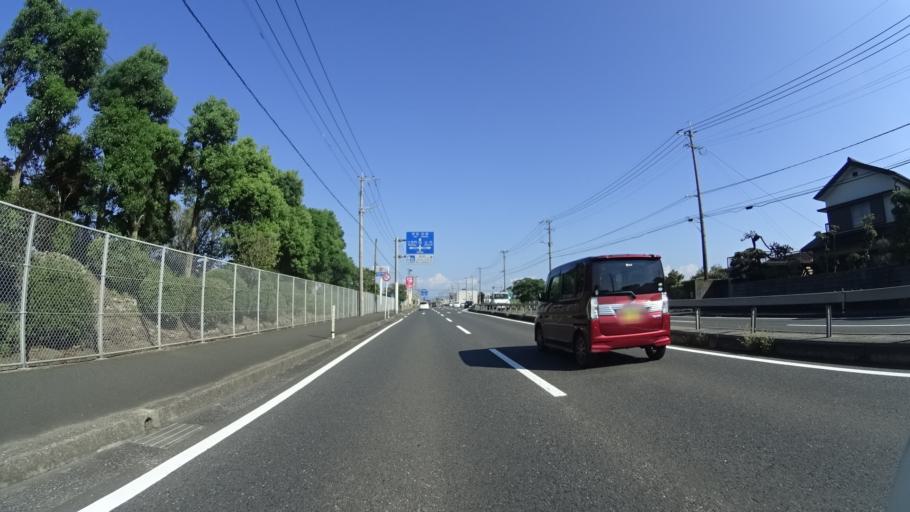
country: JP
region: Fukuoka
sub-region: Buzen-shi
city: Buzen
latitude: 33.5975
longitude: 131.1351
